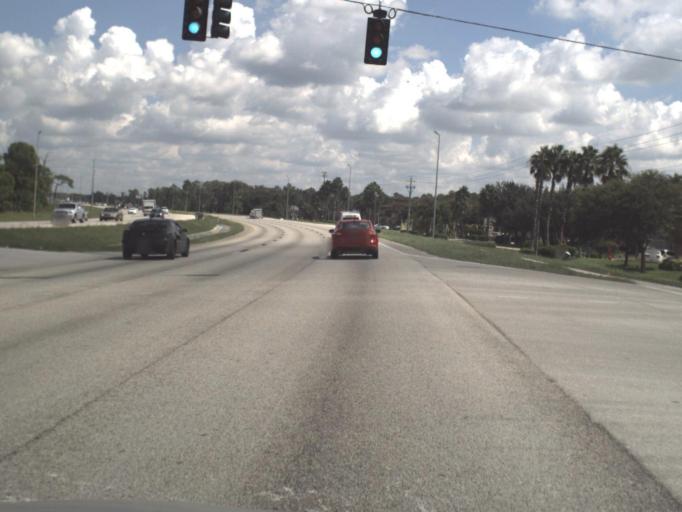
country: US
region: Florida
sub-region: Lee County
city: Fort Myers
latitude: 26.5981
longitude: -81.8356
